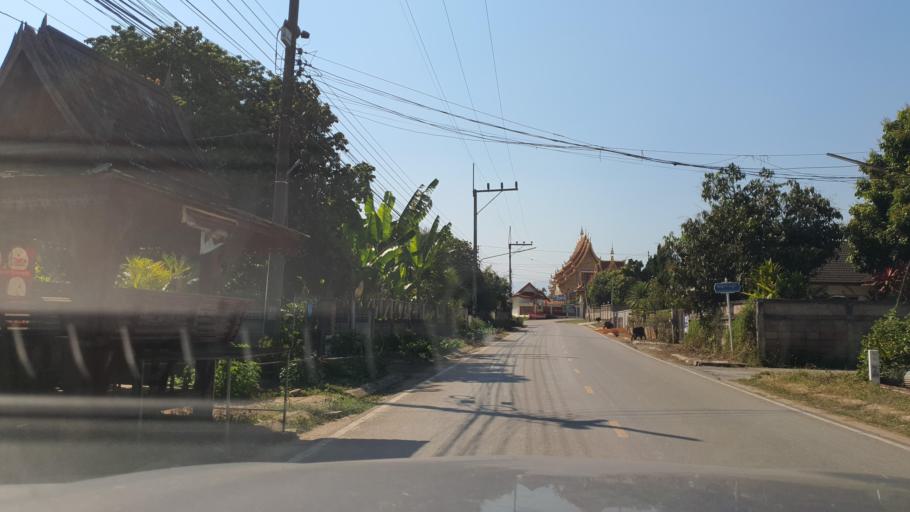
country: TH
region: Chiang Rai
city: Mae Lao
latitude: 19.7642
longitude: 99.7323
